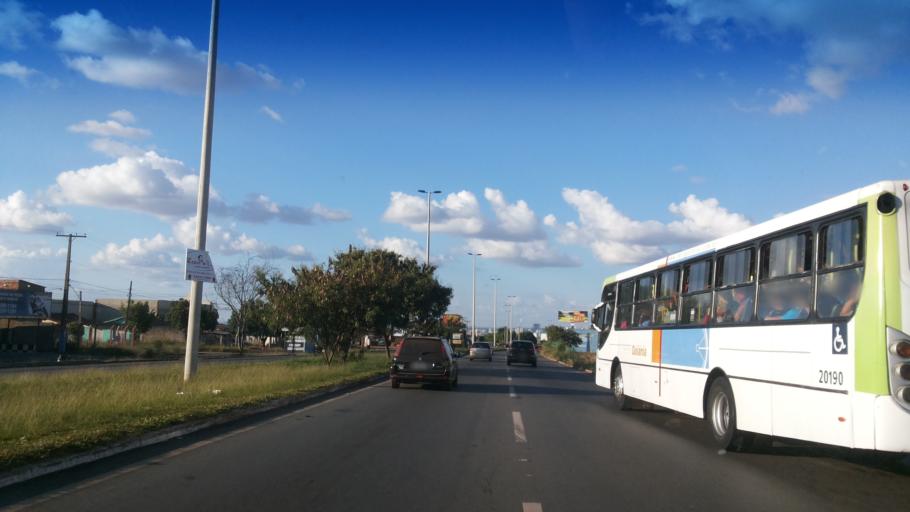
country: BR
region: Goias
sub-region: Goiania
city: Goiania
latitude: -16.7516
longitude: -49.3349
